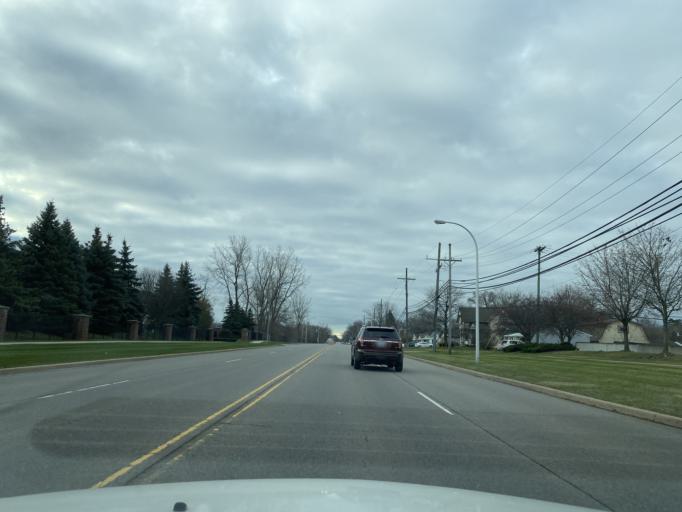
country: US
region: Michigan
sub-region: Wayne County
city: Taylor
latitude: 42.2084
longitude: -83.2876
